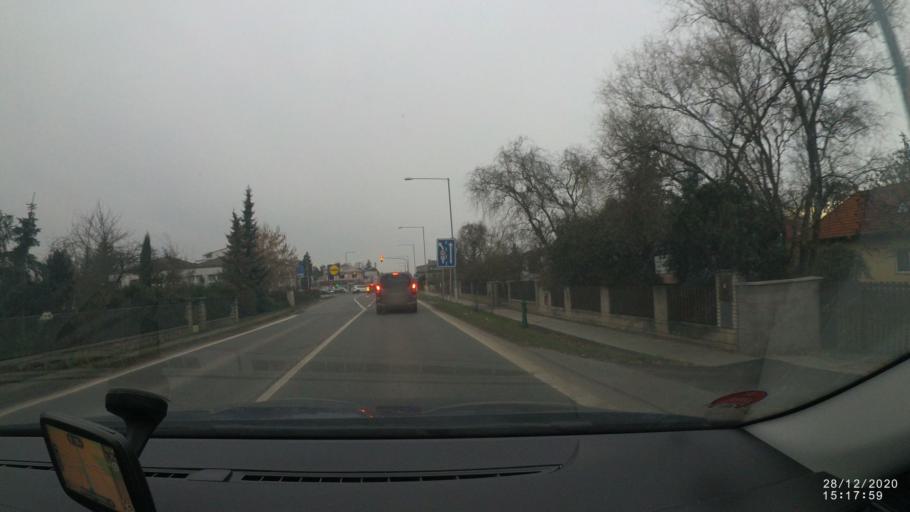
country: CZ
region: Central Bohemia
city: Sestajovice
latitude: 50.0759
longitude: 14.6621
